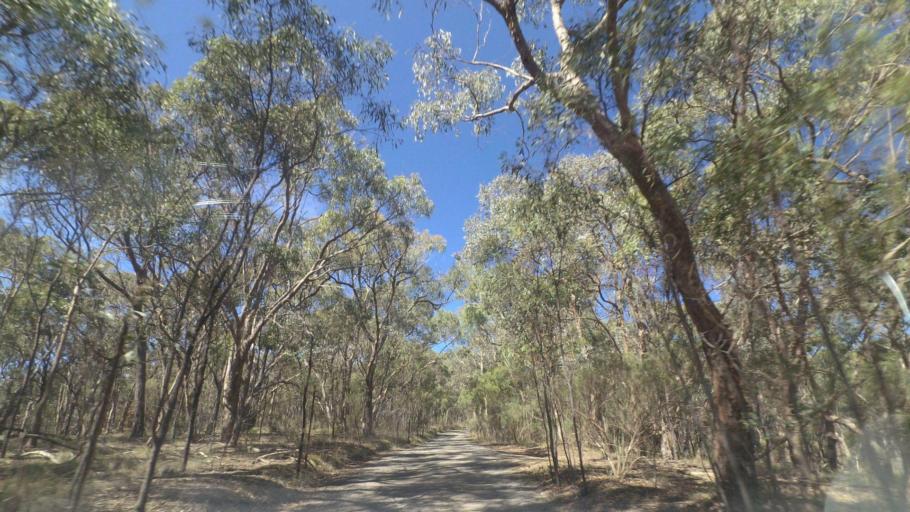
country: AU
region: Victoria
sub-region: Manningham
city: Warrandyte
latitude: -37.7497
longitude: 145.2257
